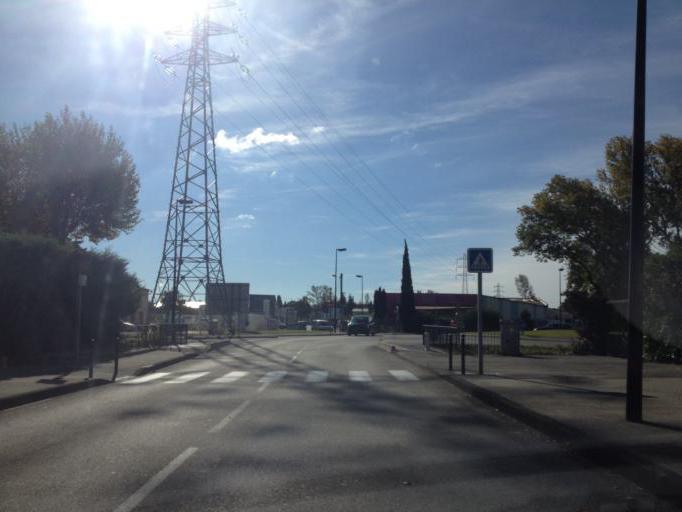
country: FR
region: Provence-Alpes-Cote d'Azur
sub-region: Departement du Vaucluse
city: Orange
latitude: 44.1269
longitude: 4.8388
